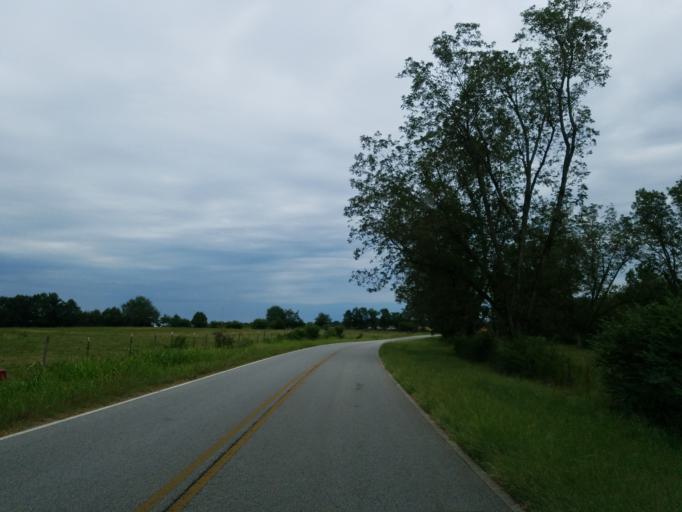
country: US
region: Georgia
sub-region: Lamar County
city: Barnesville
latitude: 33.0087
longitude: -84.0807
